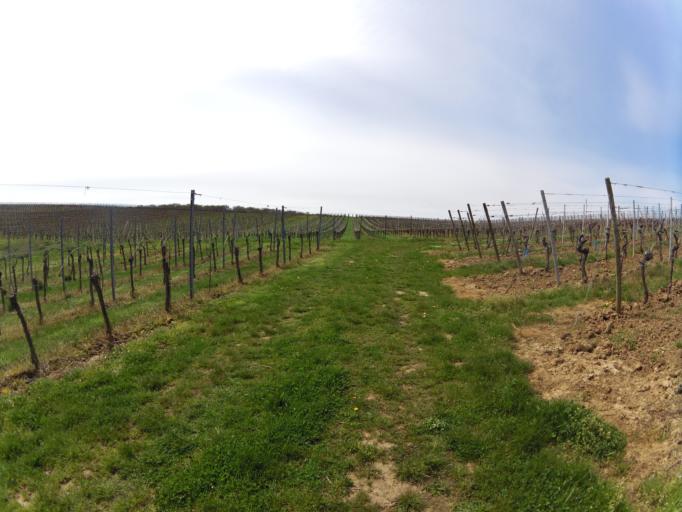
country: DE
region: Bavaria
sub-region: Regierungsbezirk Unterfranken
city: Nordheim
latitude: 49.8618
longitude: 10.1615
